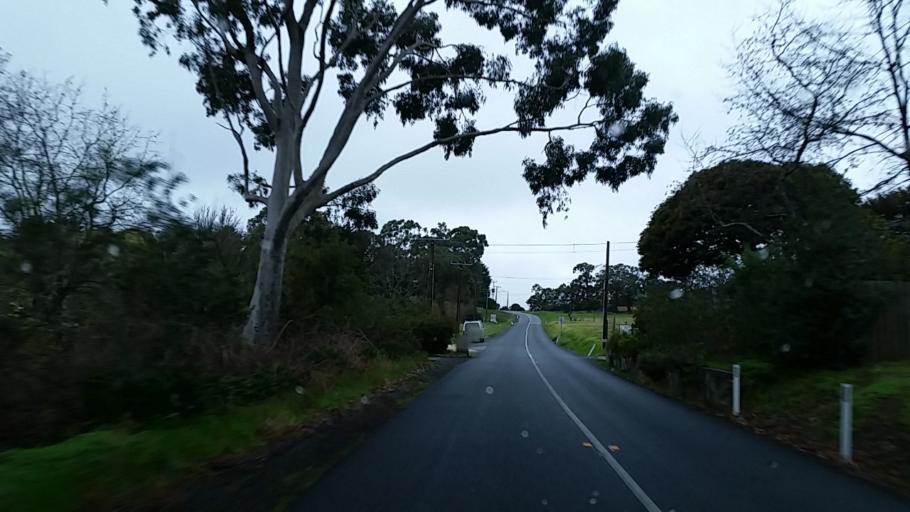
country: AU
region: South Australia
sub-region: Adelaide Hills
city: Bridgewater
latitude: -34.9563
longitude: 138.7515
